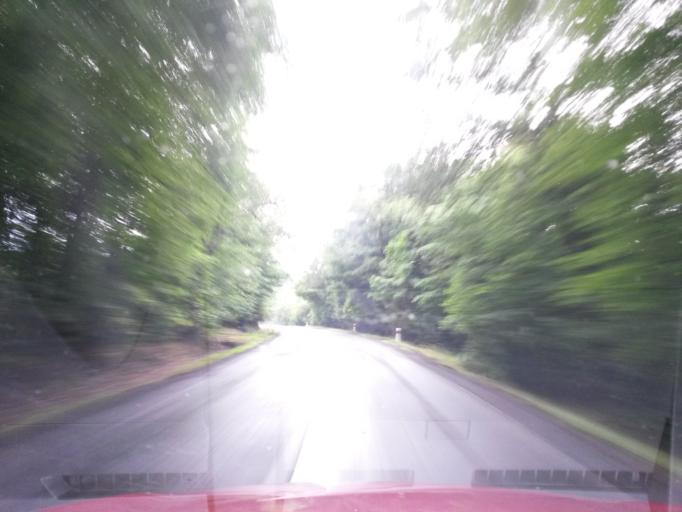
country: SK
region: Banskobystricky
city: Krupina
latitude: 48.2056
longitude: 19.0747
